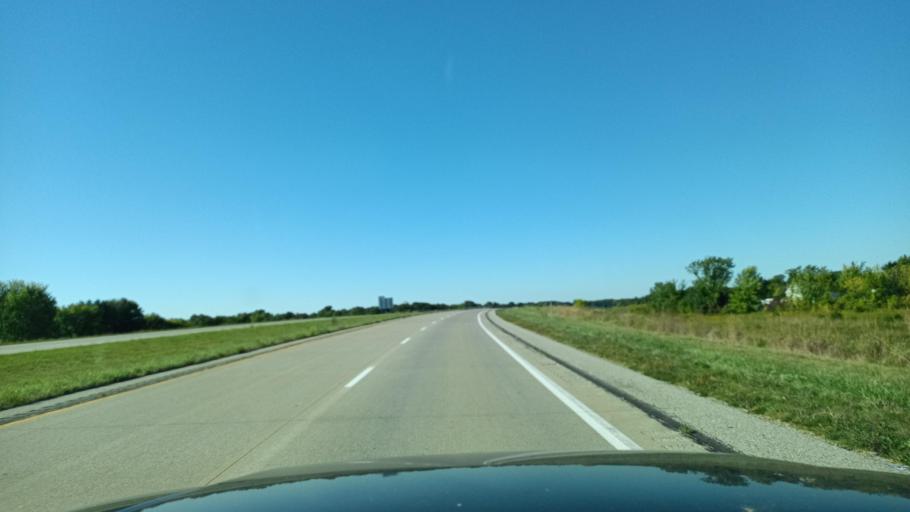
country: US
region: Iowa
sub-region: Lee County
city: Fort Madison
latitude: 40.6523
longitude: -91.3634
